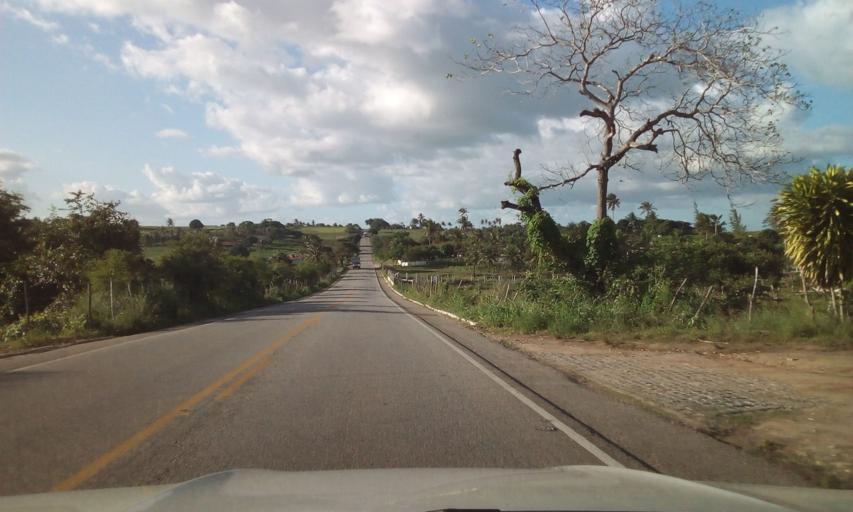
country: BR
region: Paraiba
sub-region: Pilar
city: Pilar
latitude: -7.1858
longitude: -35.2313
